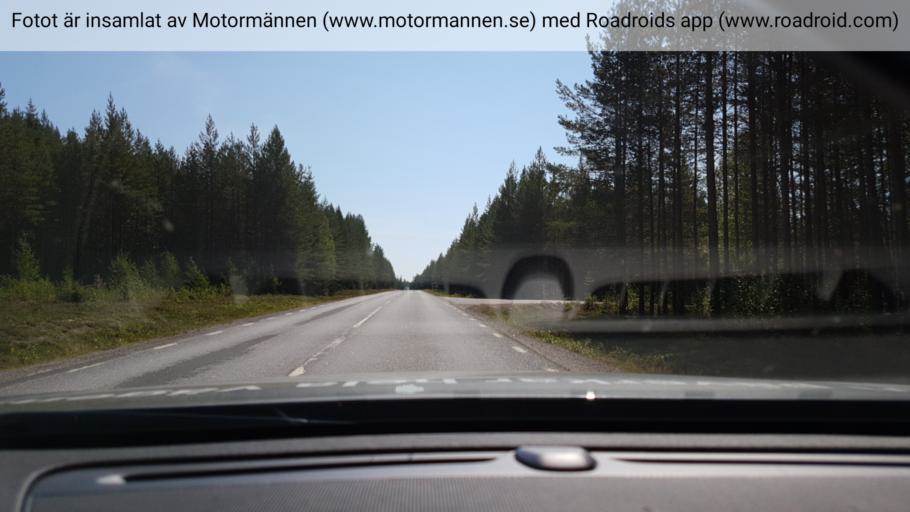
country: SE
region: Vaesterbotten
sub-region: Vindelns Kommun
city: Vindeln
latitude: 64.2546
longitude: 19.6343
